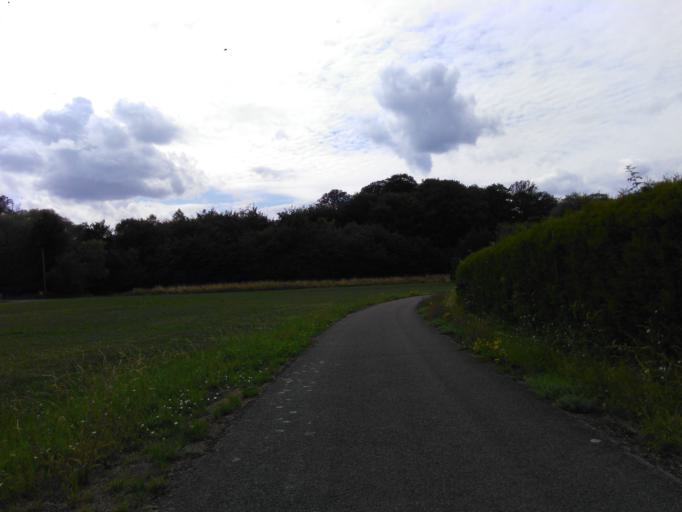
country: LU
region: Grevenmacher
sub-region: Canton d'Echternach
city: Consdorf
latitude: 49.7627
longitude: 6.3481
